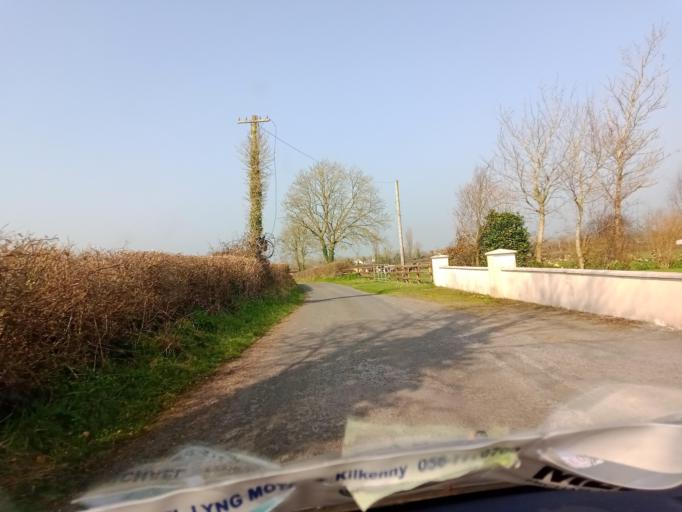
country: IE
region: Leinster
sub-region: Kilkenny
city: Callan
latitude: 52.5210
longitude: -7.4085
